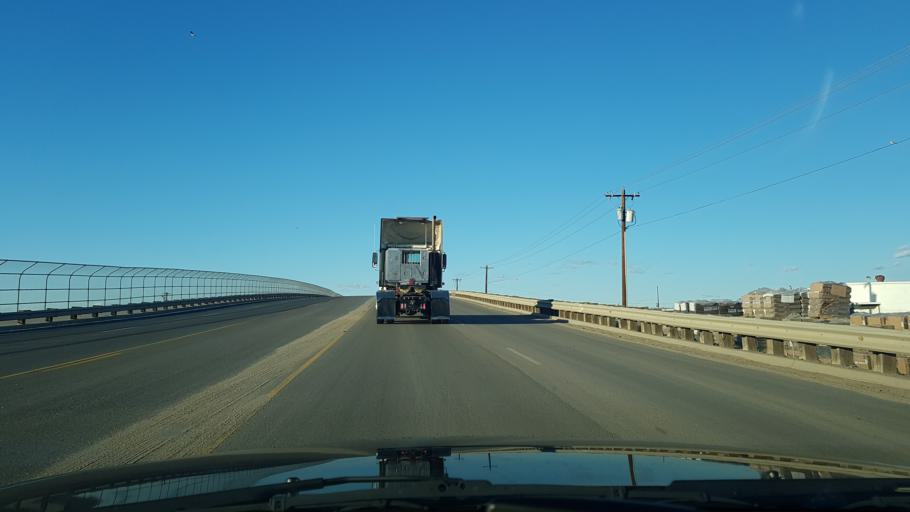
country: US
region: Arizona
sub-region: Yuma County
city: Yuma
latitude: 32.6861
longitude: -114.5988
